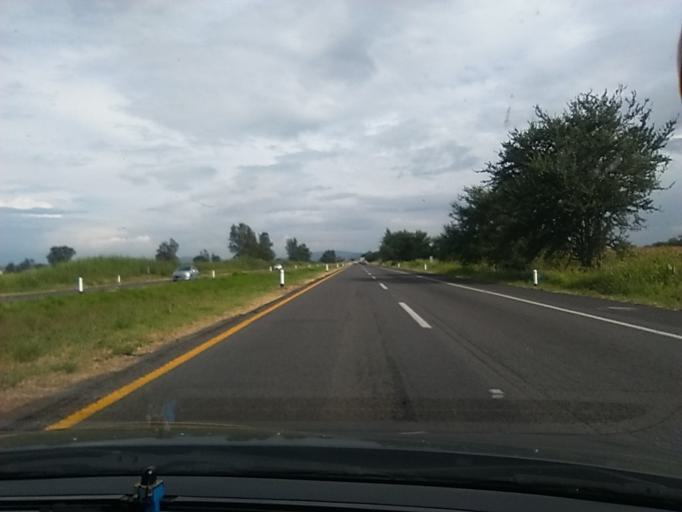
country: MX
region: Michoacan
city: Vistahermosa de Negrete
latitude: 20.3159
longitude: -102.5001
